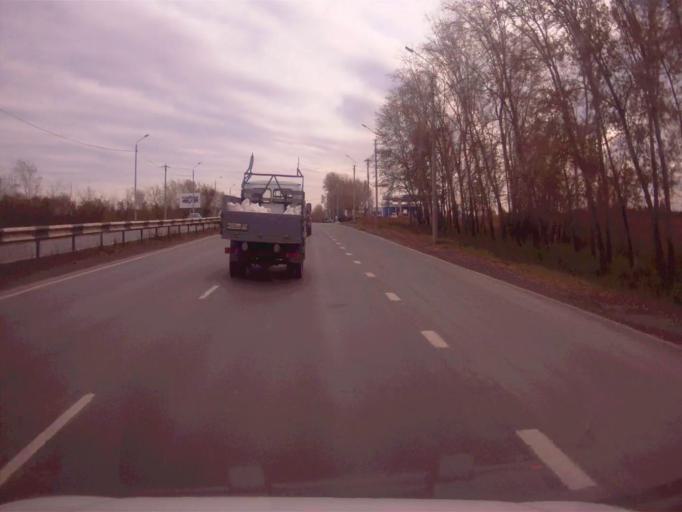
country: RU
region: Chelyabinsk
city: Novosineglazovskiy
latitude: 55.0565
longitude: 61.4062
